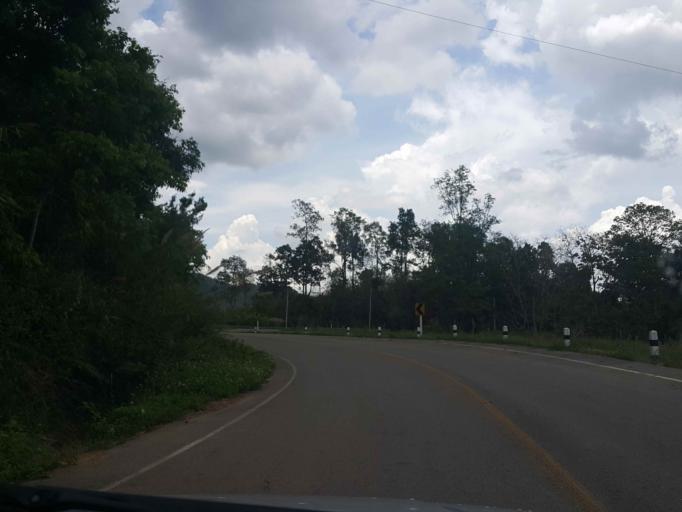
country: TH
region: Lampang
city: Ngao
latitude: 18.9343
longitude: 100.0879
